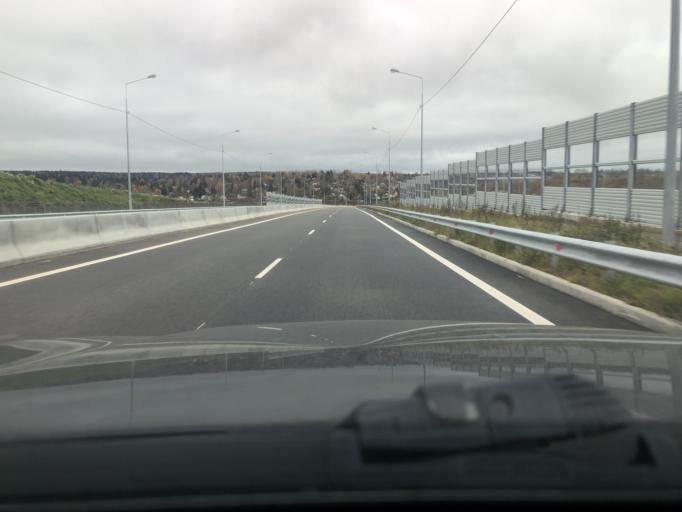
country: RU
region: Moskovskaya
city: Sergiyev Posad
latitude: 56.2959
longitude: 38.1029
